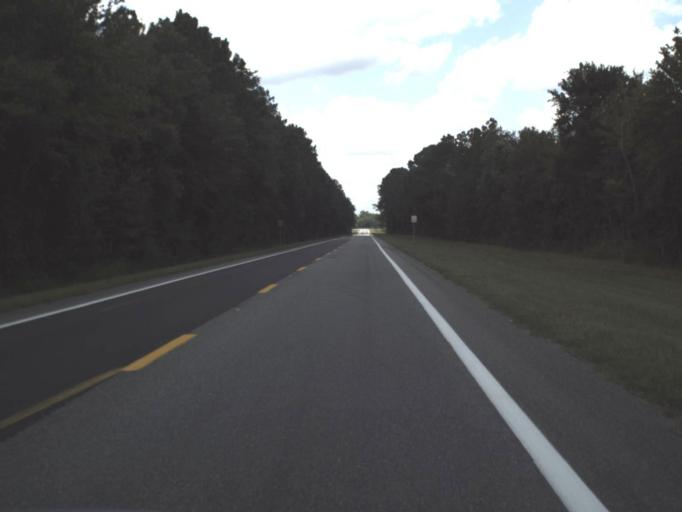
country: US
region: Florida
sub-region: Union County
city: Lake Butler
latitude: 30.0896
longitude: -82.2160
